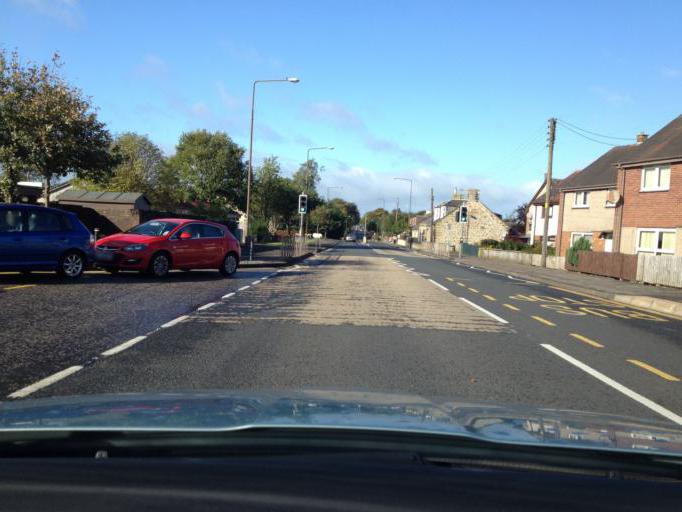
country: GB
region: Scotland
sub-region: West Lothian
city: Whitburn
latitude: 55.8689
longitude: -3.6601
